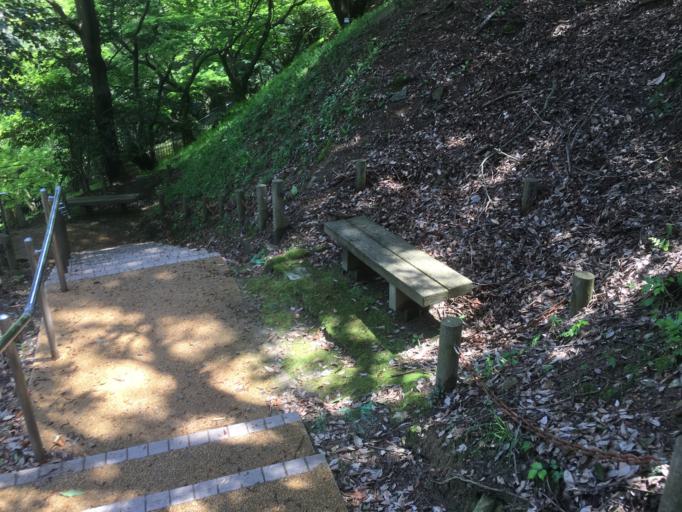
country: JP
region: Fukuoka
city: Fukuoka-shi
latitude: 33.5704
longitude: 130.3923
